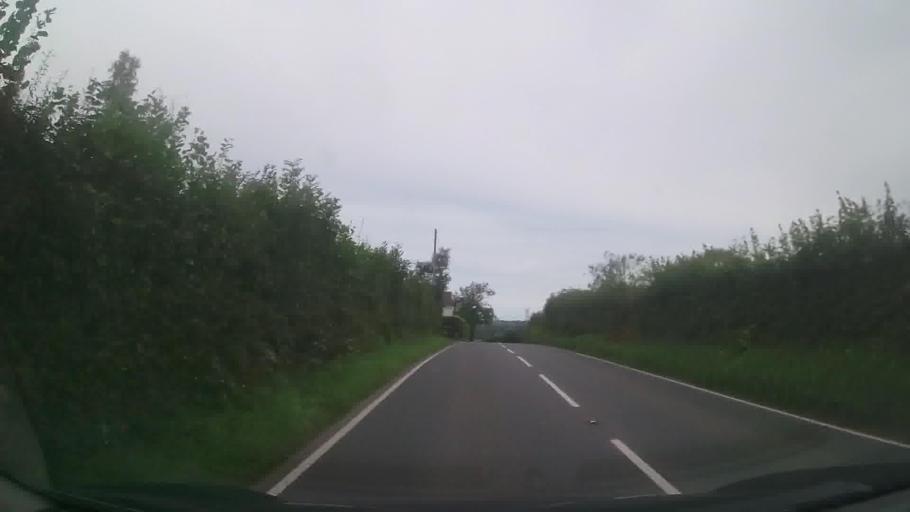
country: GB
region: Wales
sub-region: Pembrokeshire
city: Kilgetty
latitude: 51.7476
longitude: -4.7307
